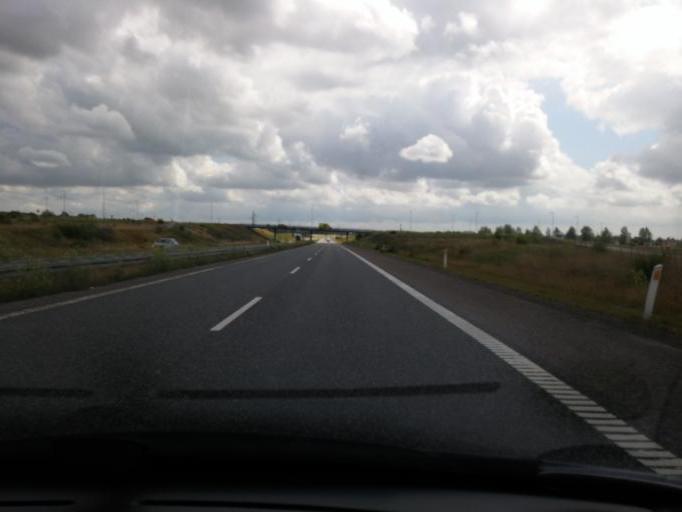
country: DK
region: South Denmark
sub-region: Faaborg-Midtfyn Kommune
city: Ringe
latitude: 55.1916
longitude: 10.5241
